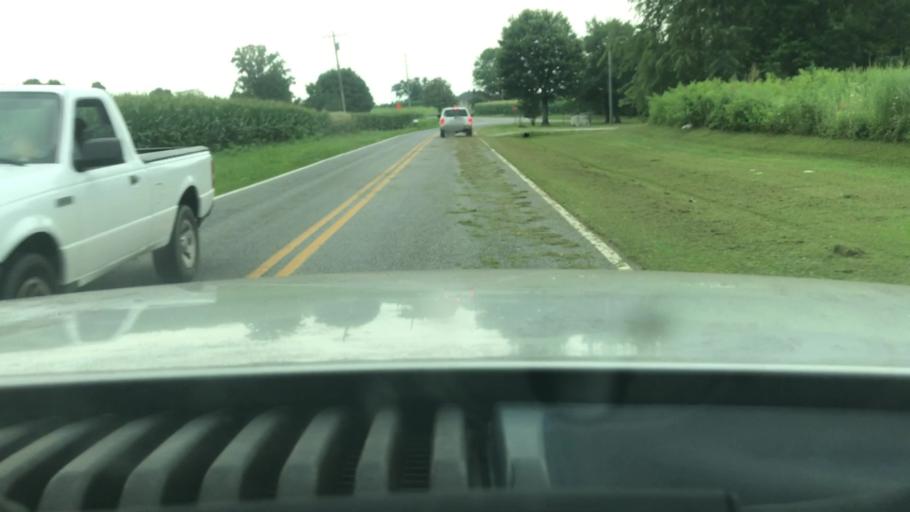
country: US
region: North Carolina
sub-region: Surry County
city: Dobson
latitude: 36.3983
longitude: -80.7980
